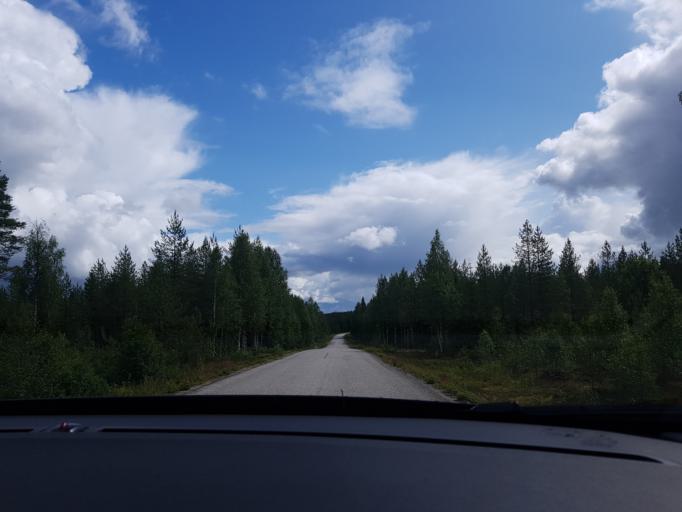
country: FI
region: Kainuu
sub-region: Kehys-Kainuu
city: Kuhmo
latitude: 64.4508
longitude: 29.6748
